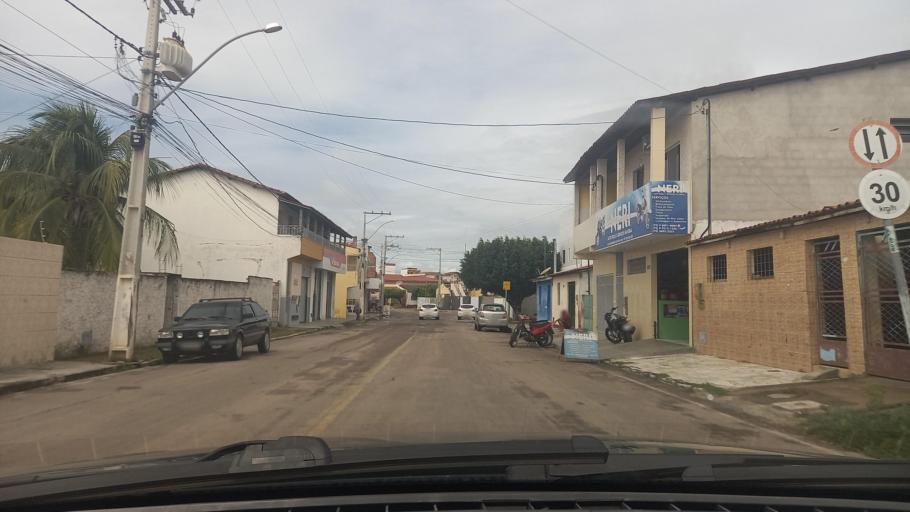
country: BR
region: Bahia
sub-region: Paulo Afonso
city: Paulo Afonso
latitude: -9.4439
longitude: -38.2188
